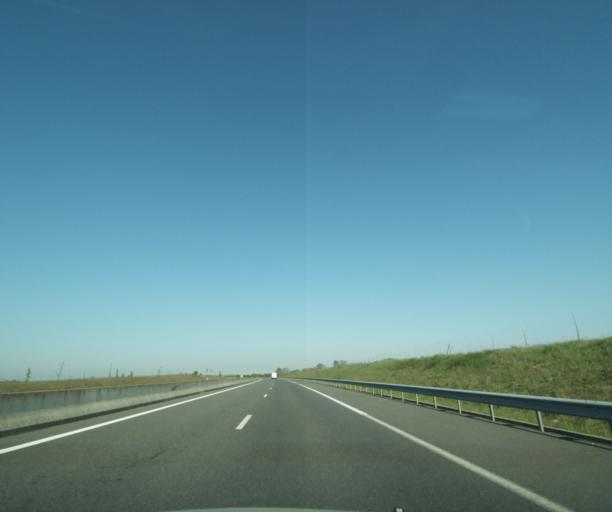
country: FR
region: Centre
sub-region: Departement du Loiret
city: Beaune-la-Rolande
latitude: 48.0923
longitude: 2.4224
